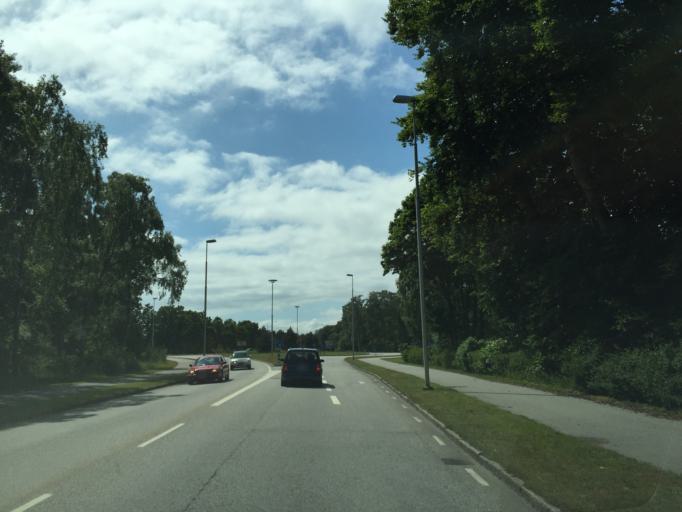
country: SE
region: Skane
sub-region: Ystads Kommun
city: Ystad
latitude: 55.4302
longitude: 13.8453
